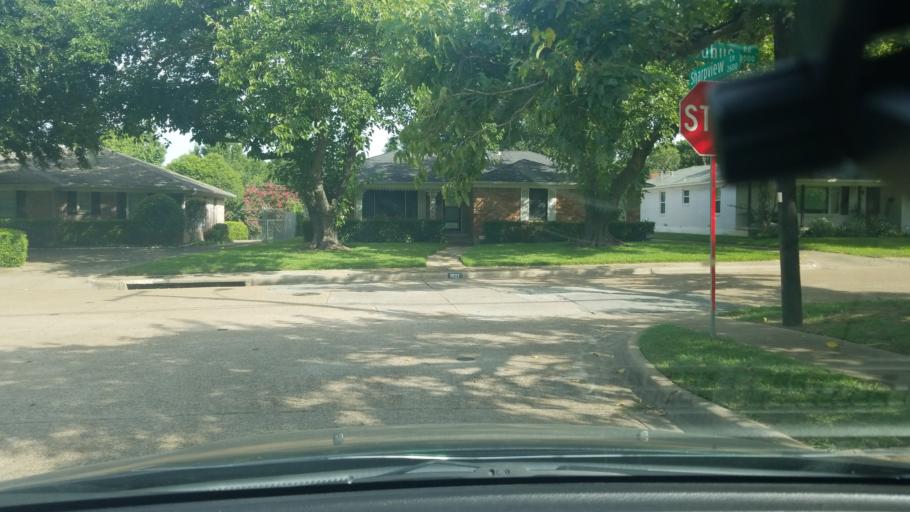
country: US
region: Texas
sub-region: Dallas County
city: Highland Park
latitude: 32.7964
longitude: -96.7068
